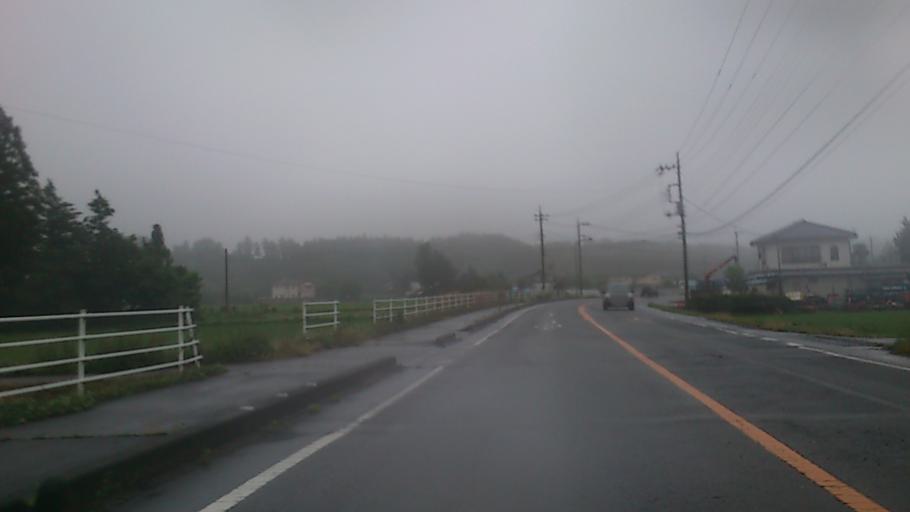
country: JP
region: Tochigi
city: Otawara
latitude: 36.8291
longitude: 140.0773
